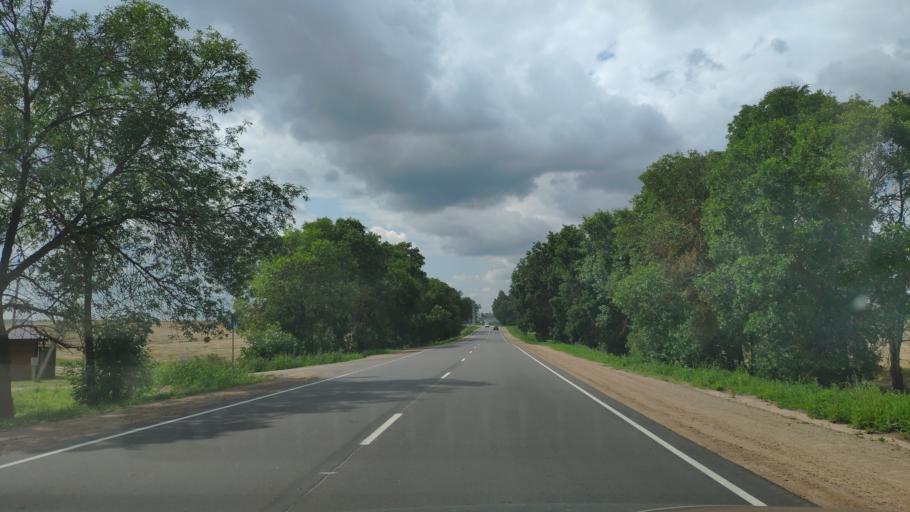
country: BY
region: Minsk
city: Zaslawye
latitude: 54.0069
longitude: 27.3258
